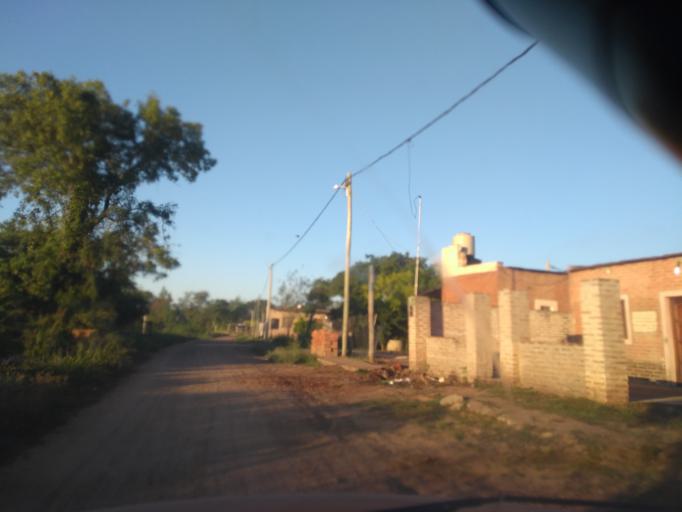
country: AR
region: Chaco
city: Resistencia
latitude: -27.4577
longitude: -58.9680
